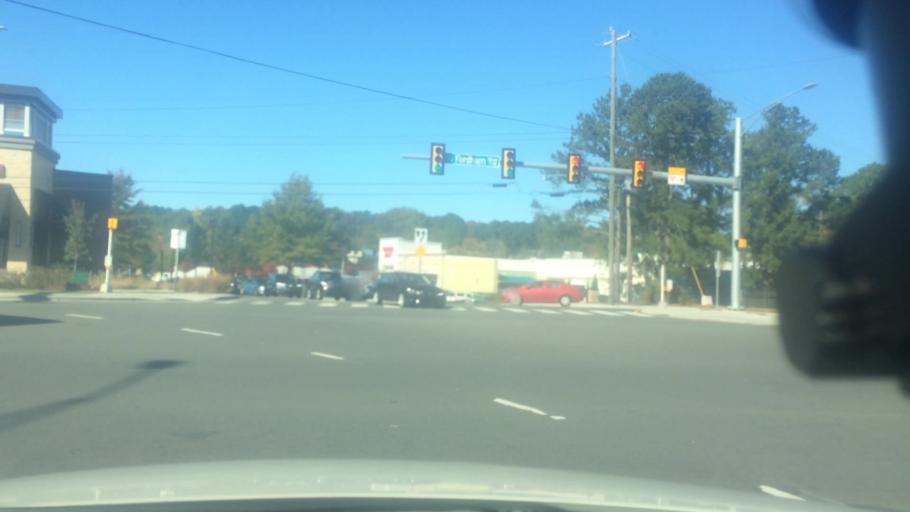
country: US
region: North Carolina
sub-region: Orange County
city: Chapel Hill
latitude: 35.9363
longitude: -79.0233
